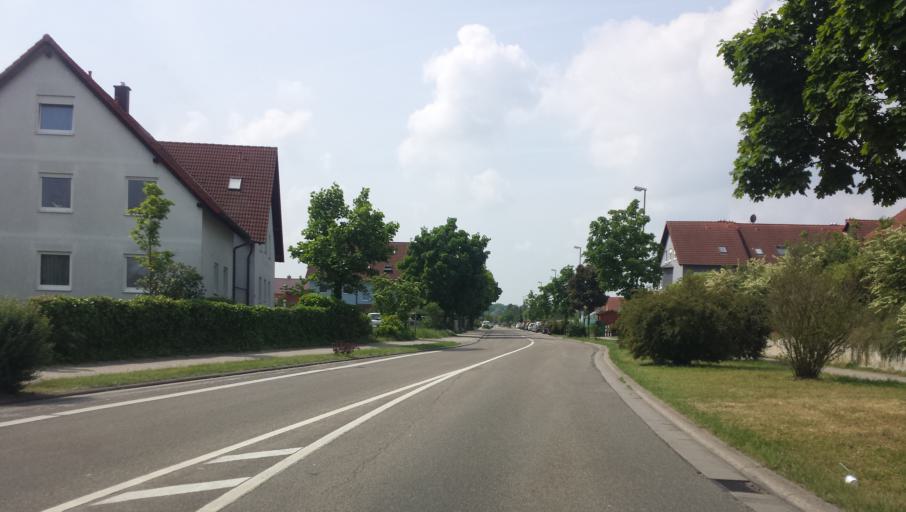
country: DE
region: Rheinland-Pfalz
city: Germersheim
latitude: 49.1977
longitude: 8.3600
